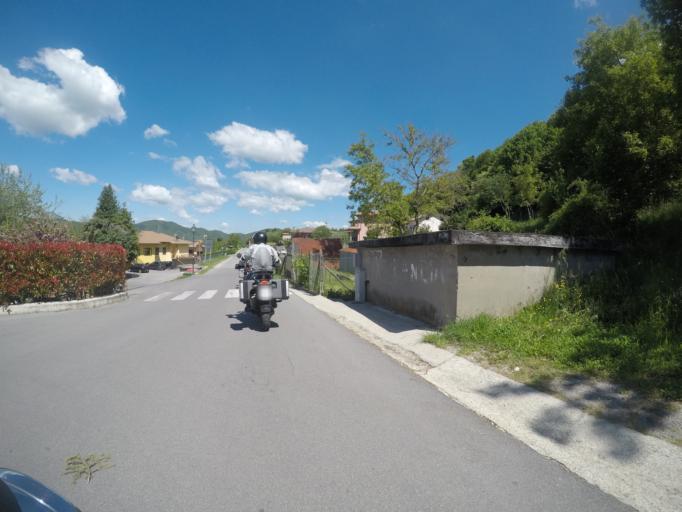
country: IT
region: Tuscany
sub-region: Provincia di Lucca
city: Careggine
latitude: 44.1177
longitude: 10.3290
